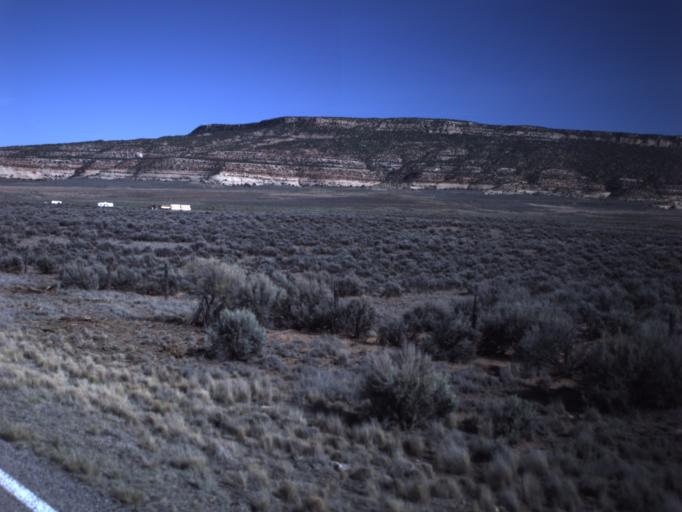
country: US
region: Utah
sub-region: San Juan County
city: Monticello
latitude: 38.0731
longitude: -109.3545
